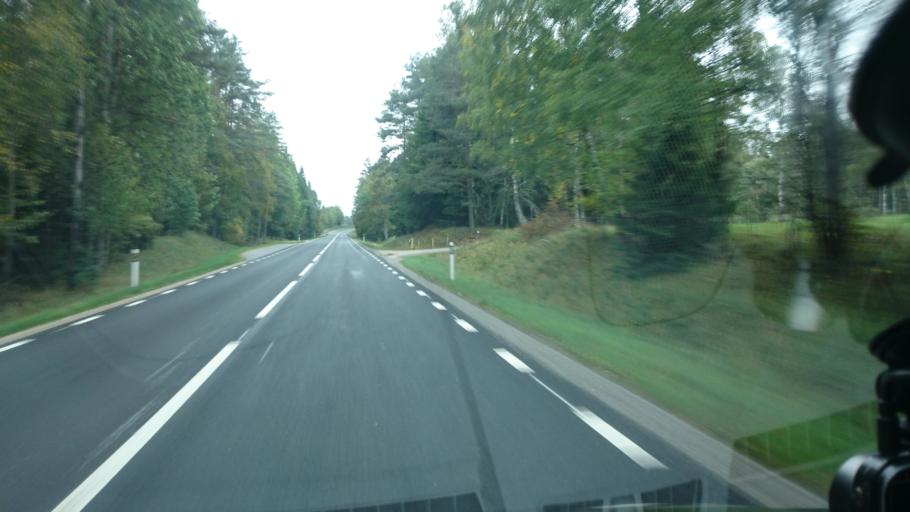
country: SE
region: Vaestra Goetaland
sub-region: Svenljunga Kommun
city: Svenljunga
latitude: 57.5415
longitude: 13.1215
